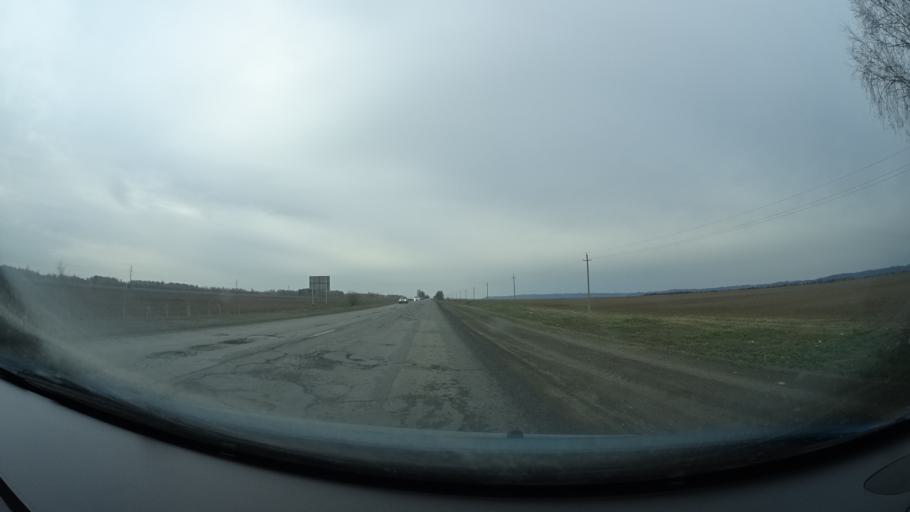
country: RU
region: Perm
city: Ust'-Kachka
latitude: 58.0658
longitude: 55.6227
